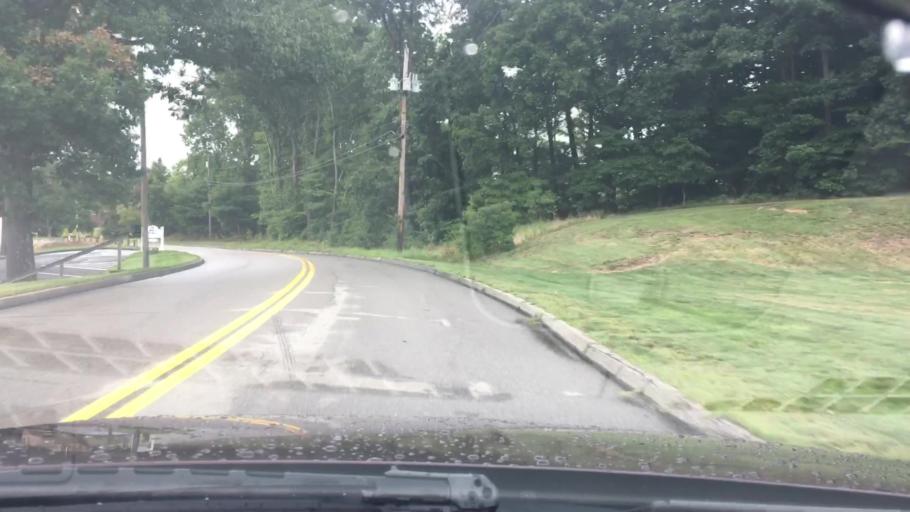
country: US
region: Connecticut
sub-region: Hartford County
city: Glastonbury Center
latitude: 41.7111
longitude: -72.5791
